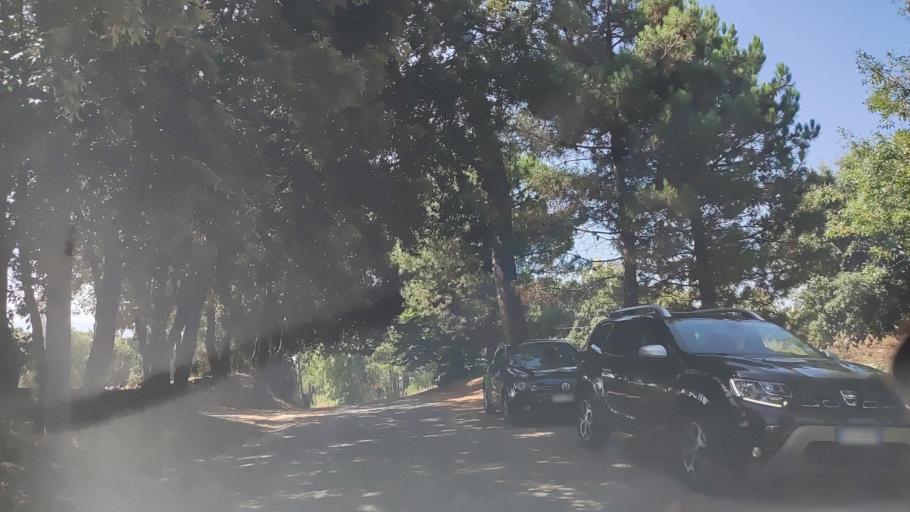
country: IT
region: Calabria
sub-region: Provincia di Reggio Calabria
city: Seminara
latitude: 38.3468
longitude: 15.8411
